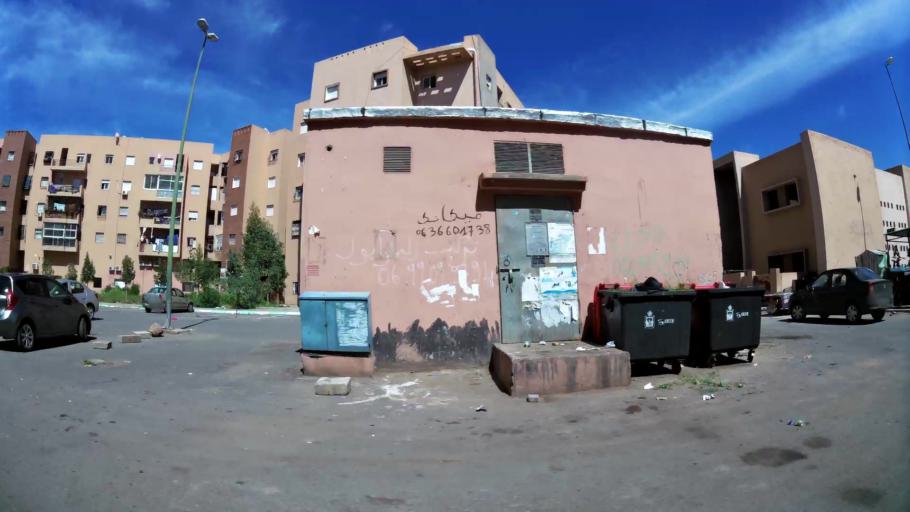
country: MA
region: Marrakech-Tensift-Al Haouz
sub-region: Marrakech
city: Marrakesh
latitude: 31.6384
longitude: -8.0757
